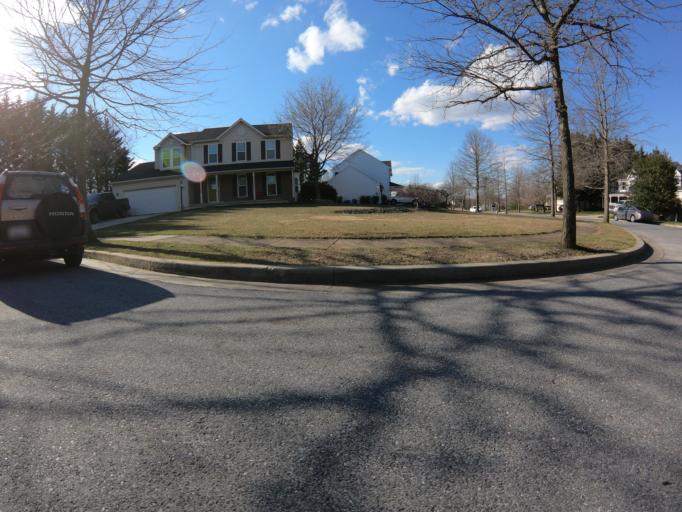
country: US
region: Maryland
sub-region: Howard County
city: Ellicott City
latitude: 39.2519
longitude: -76.8030
